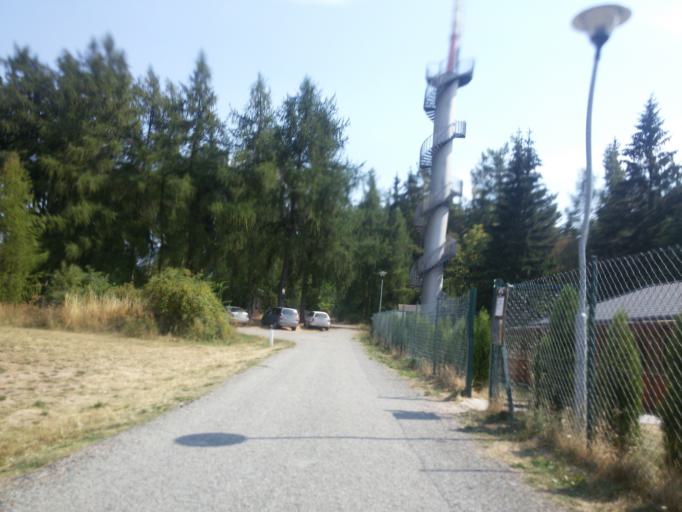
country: CZ
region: South Moravian
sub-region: Okres Brno-Venkov
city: Lomnice
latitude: 49.4442
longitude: 16.4636
